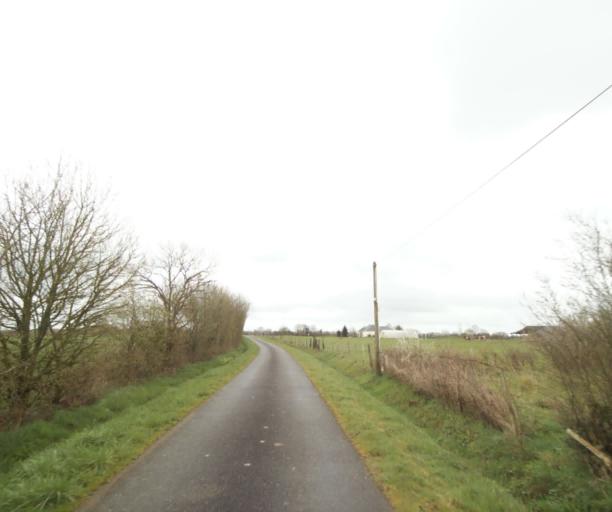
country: FR
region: Pays de la Loire
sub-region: Departement de la Loire-Atlantique
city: Bouvron
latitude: 47.4531
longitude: -1.8918
